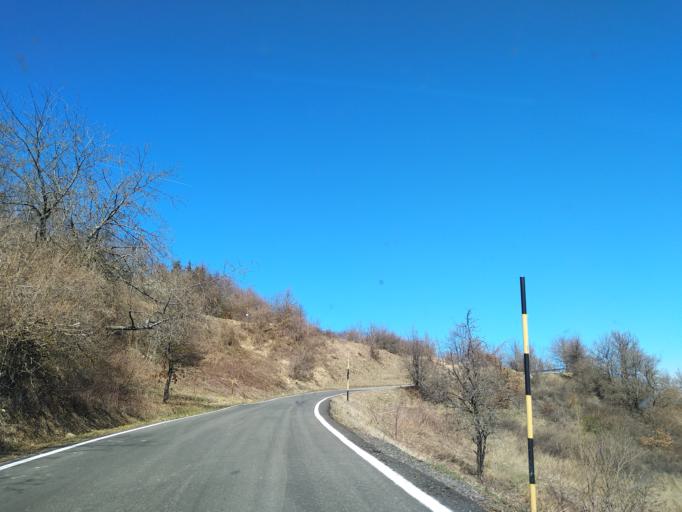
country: IT
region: Emilia-Romagna
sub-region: Provincia di Reggio Emilia
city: Ramiseto
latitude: 44.4040
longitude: 10.2655
